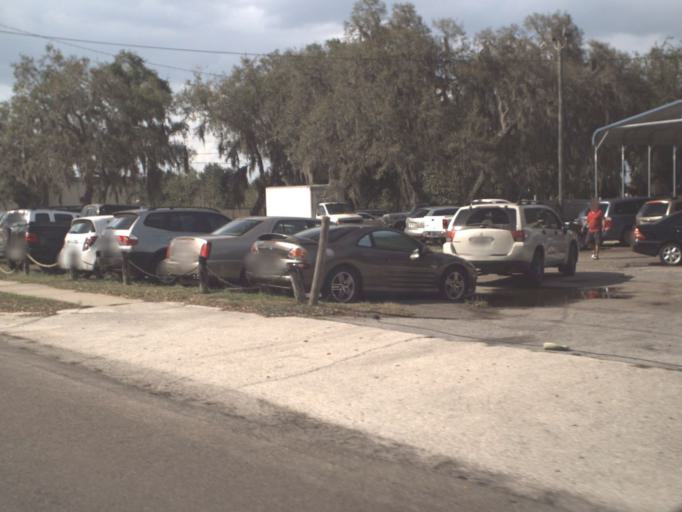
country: US
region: Florida
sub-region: Lake County
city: Eustis
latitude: 28.8631
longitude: -81.6855
